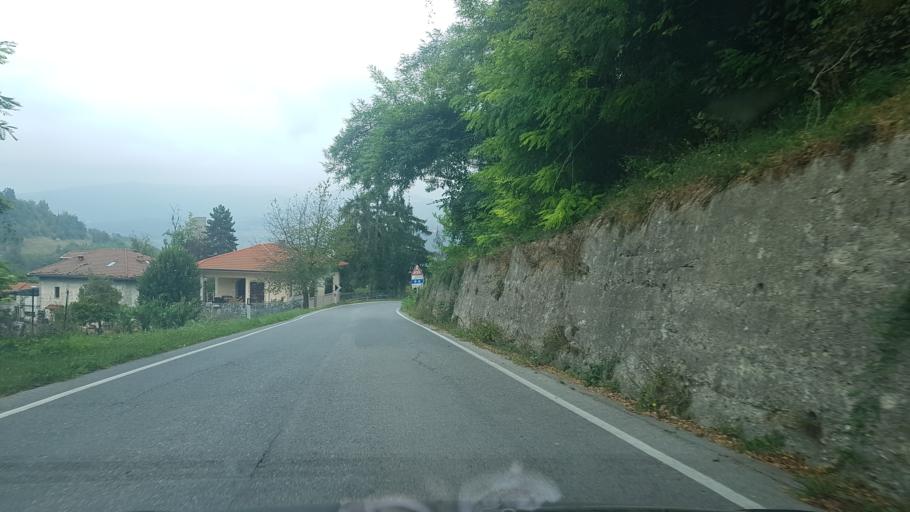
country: IT
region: Piedmont
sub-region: Provincia di Cuneo
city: Camerana
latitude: 44.4207
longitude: 8.1401
